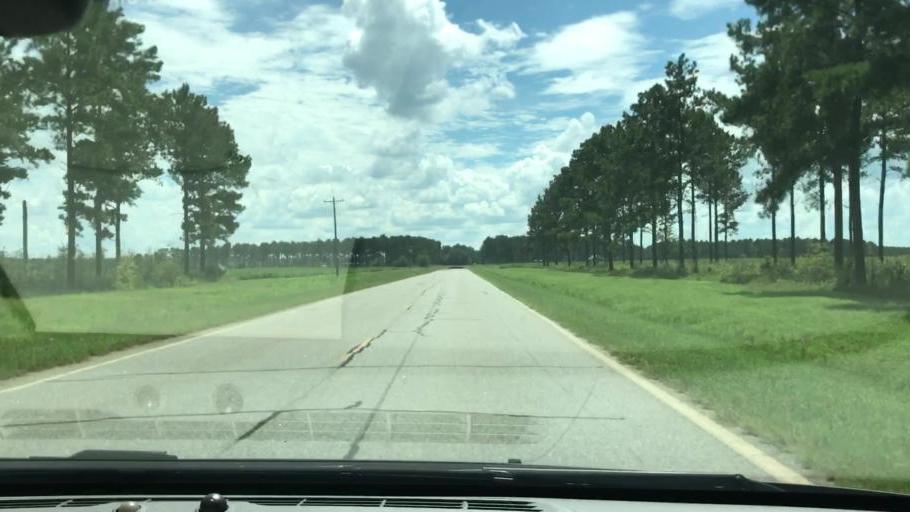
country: US
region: Georgia
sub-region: Quitman County
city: Georgetown
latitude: 32.0573
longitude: -85.0363
